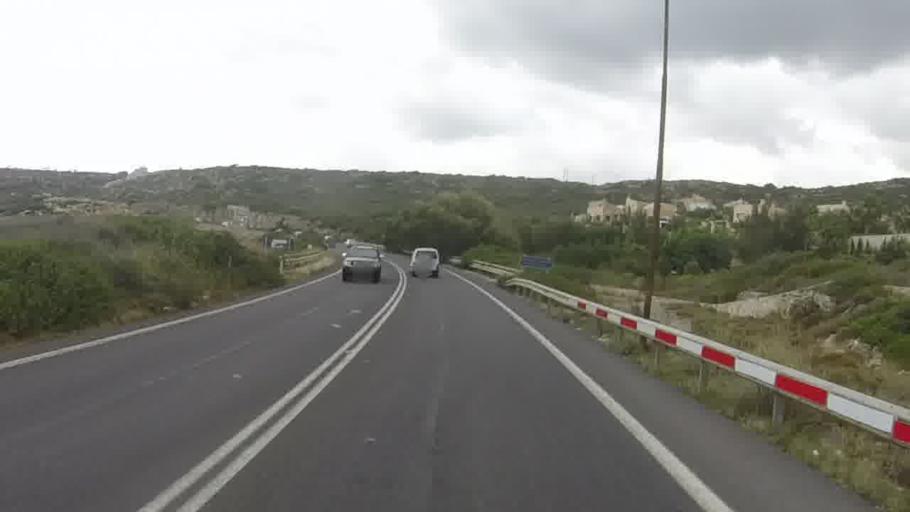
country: GR
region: Crete
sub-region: Nomos Rethymnis
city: Atsipopoulon
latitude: 35.3586
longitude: 24.4072
